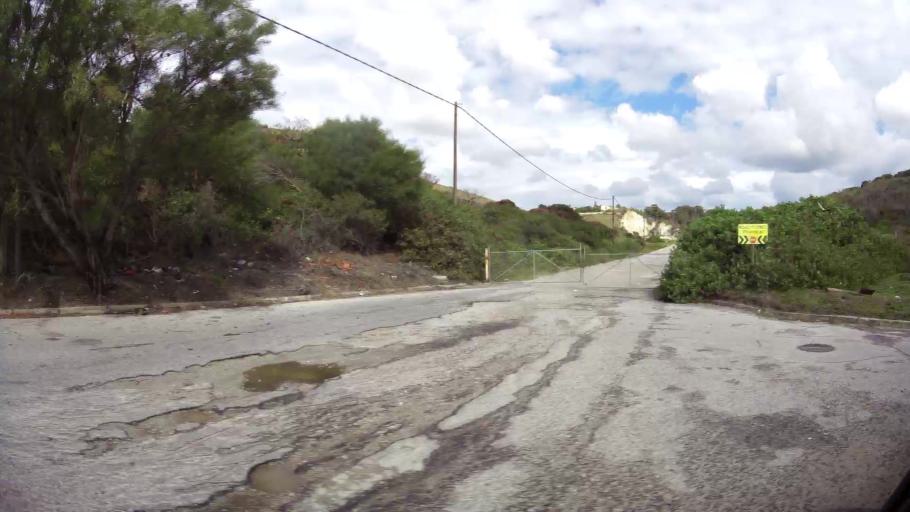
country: ZA
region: Eastern Cape
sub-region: Nelson Mandela Bay Metropolitan Municipality
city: Port Elizabeth
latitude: -33.9311
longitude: 25.5528
